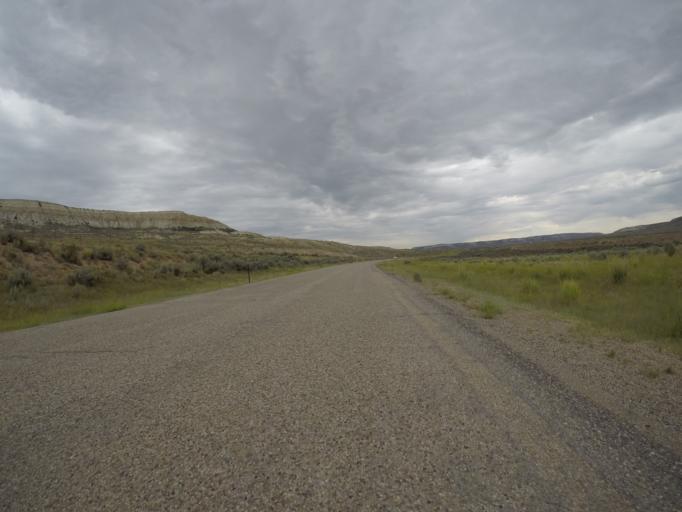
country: US
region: Wyoming
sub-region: Lincoln County
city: Kemmerer
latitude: 41.8230
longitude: -110.7369
